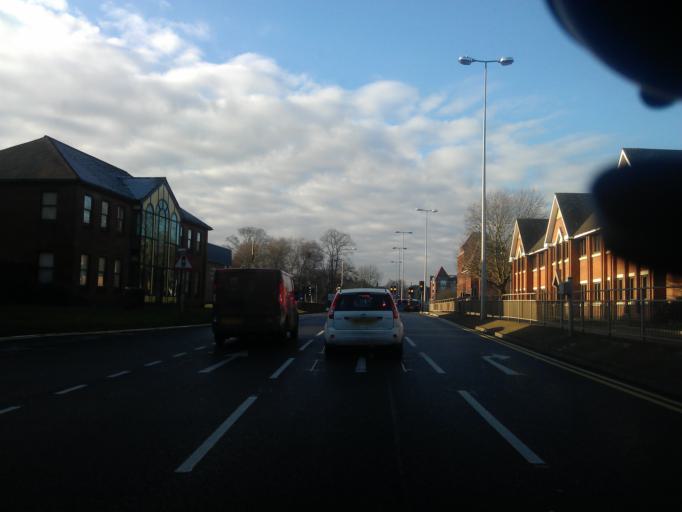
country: GB
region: England
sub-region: Essex
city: Colchester
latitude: 51.8867
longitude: 0.8969
